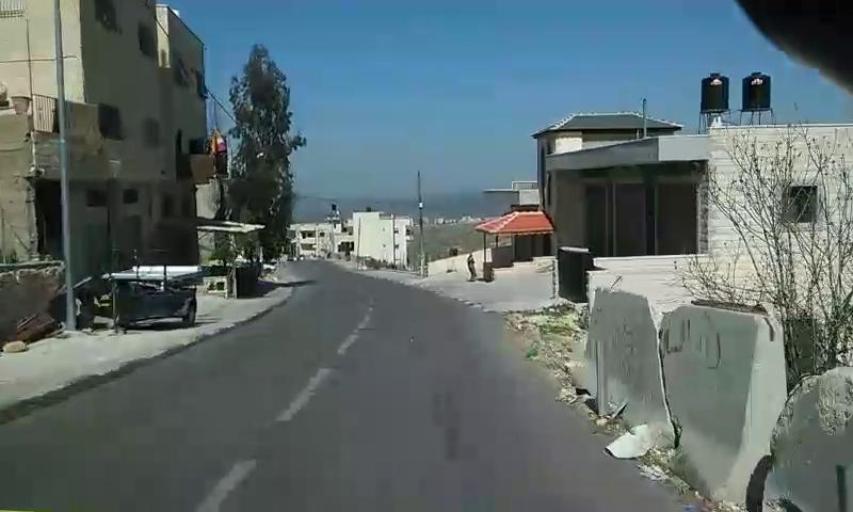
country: PS
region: West Bank
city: Husan
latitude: 31.7066
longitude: 35.1429
